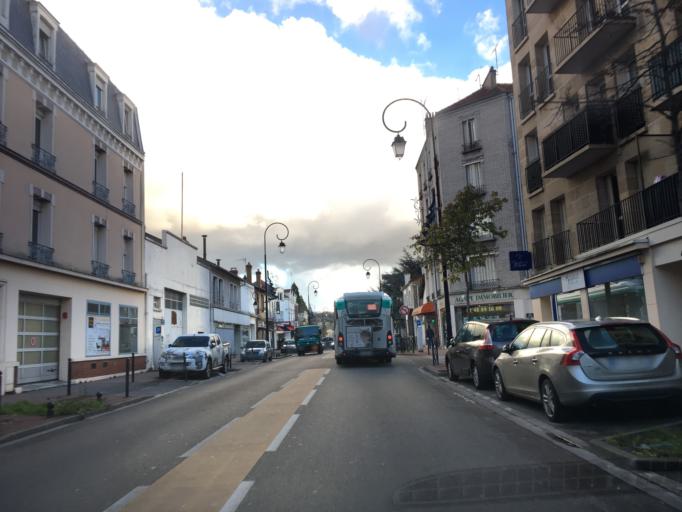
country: FR
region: Ile-de-France
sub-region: Departement du Val-de-Marne
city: Saint-Maur-des-Fosses
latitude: 48.7956
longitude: 2.5087
